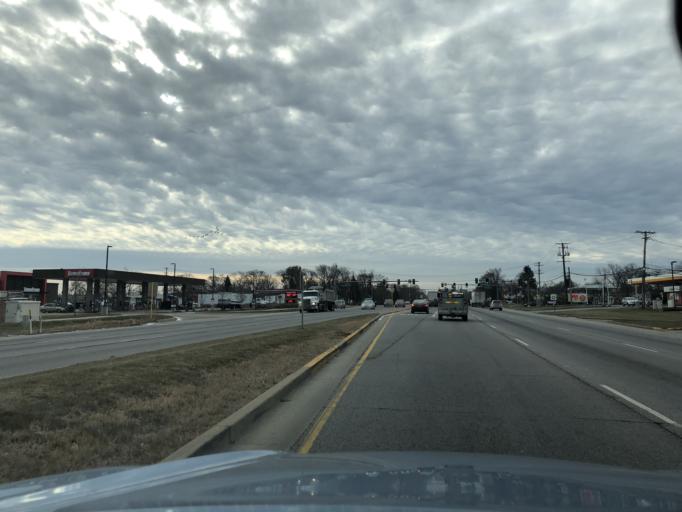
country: US
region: Illinois
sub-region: DuPage County
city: Wood Dale
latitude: 41.9733
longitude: -87.9593
